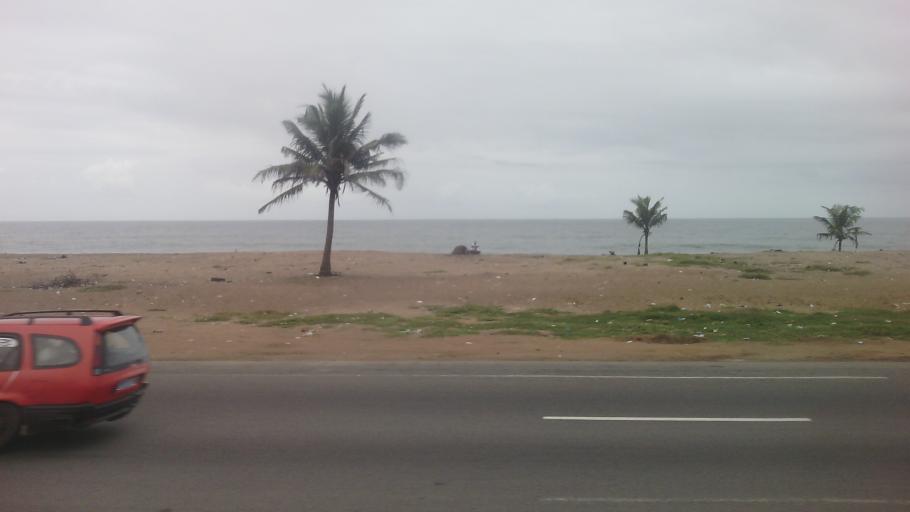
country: CI
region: Lagunes
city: Abidjan
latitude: 5.2425
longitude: -3.9168
